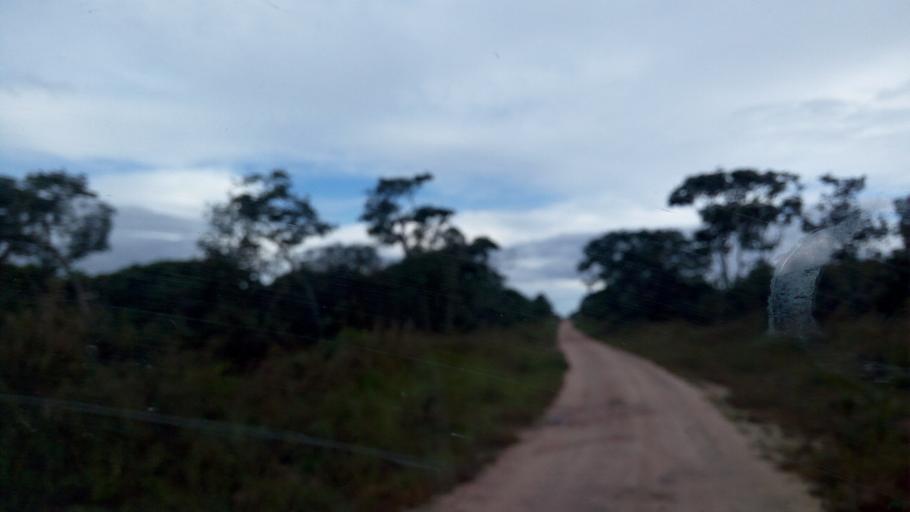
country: CD
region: Katanga
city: Kalemie
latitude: -6.5942
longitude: 29.0403
